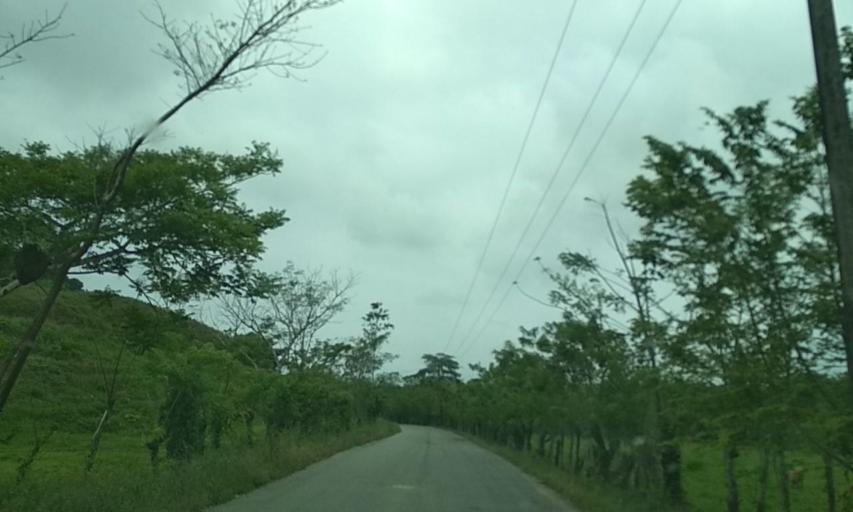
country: MX
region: Veracruz
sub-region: Uxpanapa
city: Poblado 10
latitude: 17.4699
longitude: -94.1161
